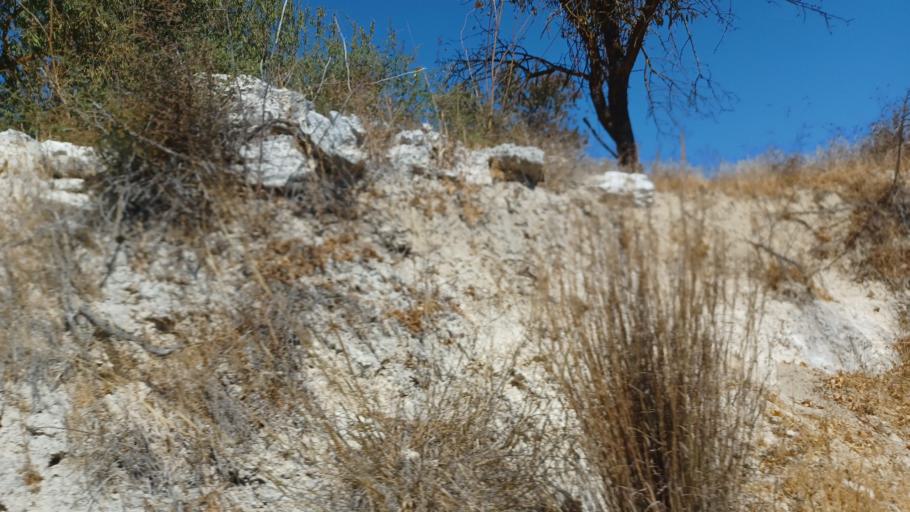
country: CY
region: Pafos
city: Mesogi
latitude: 34.8622
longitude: 32.5229
